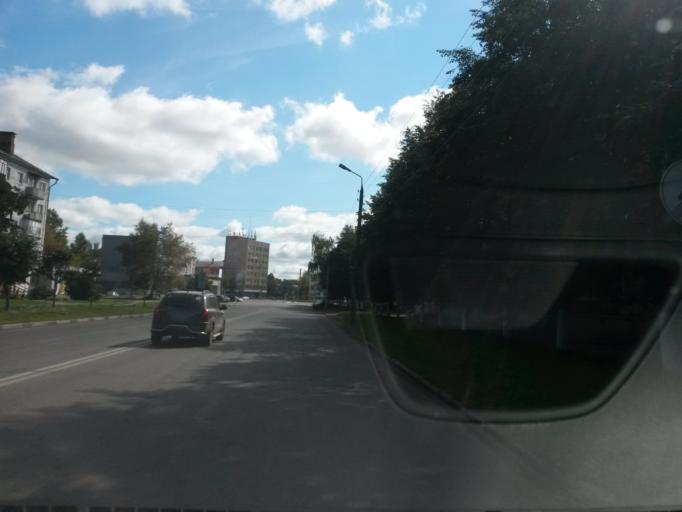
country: RU
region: Jaroslavl
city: Yaroslavl
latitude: 57.6298
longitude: 39.8447
